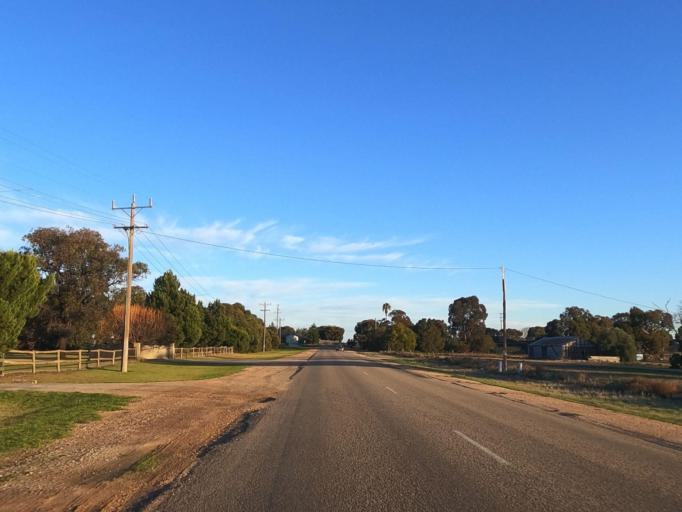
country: AU
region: Victoria
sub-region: Swan Hill
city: Swan Hill
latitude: -35.3586
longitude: 143.5521
